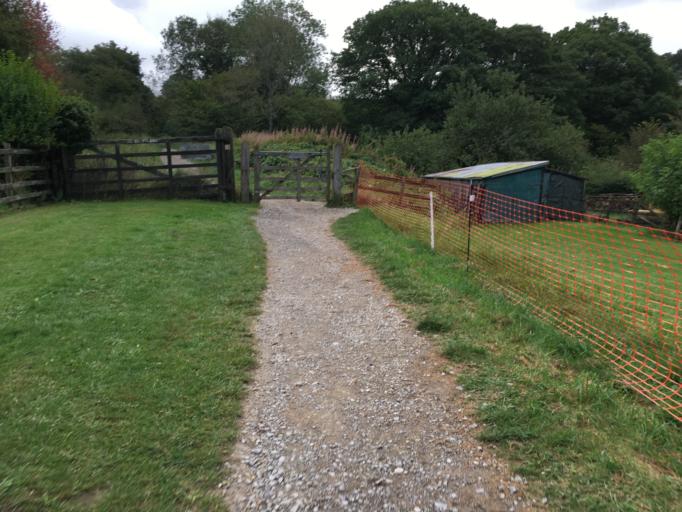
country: GB
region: England
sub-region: North Yorkshire
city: Sleights
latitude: 54.4072
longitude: -0.7350
